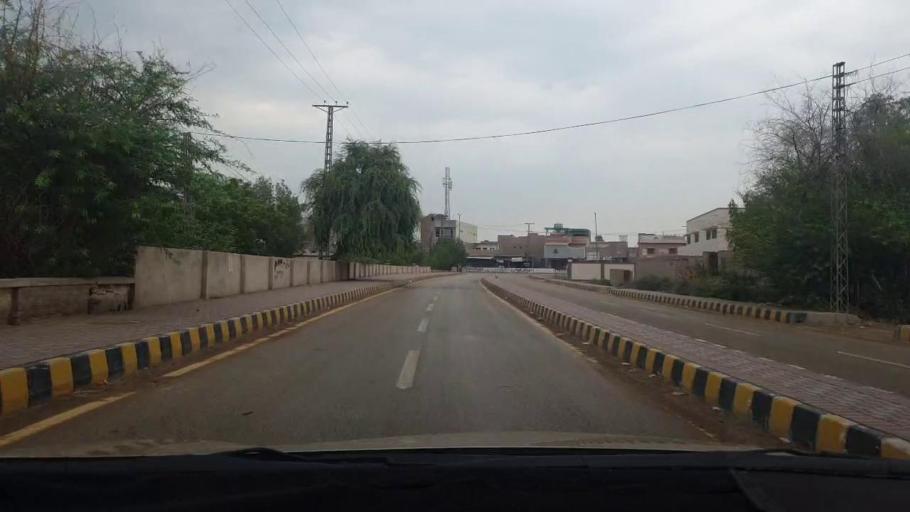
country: PK
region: Sindh
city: Larkana
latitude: 27.5653
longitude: 68.1978
